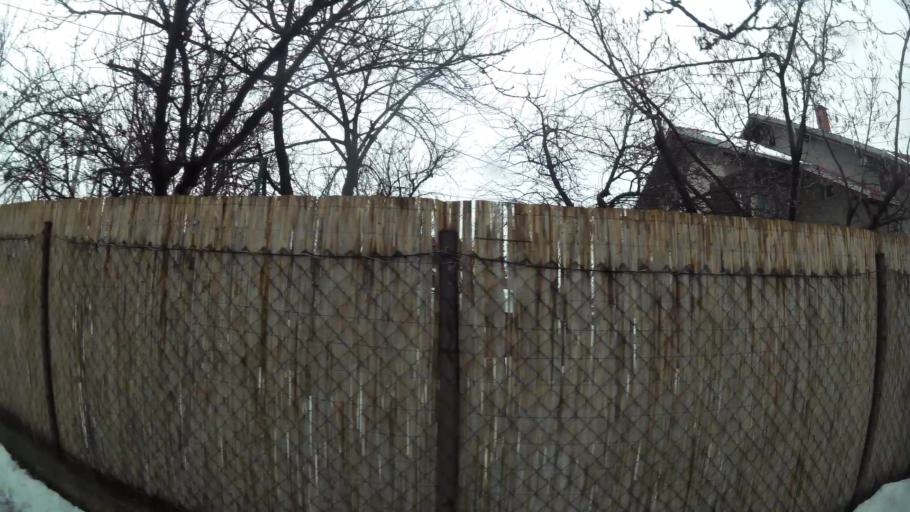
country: RS
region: Central Serbia
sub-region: Belgrade
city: Zemun
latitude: 44.8413
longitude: 20.3609
